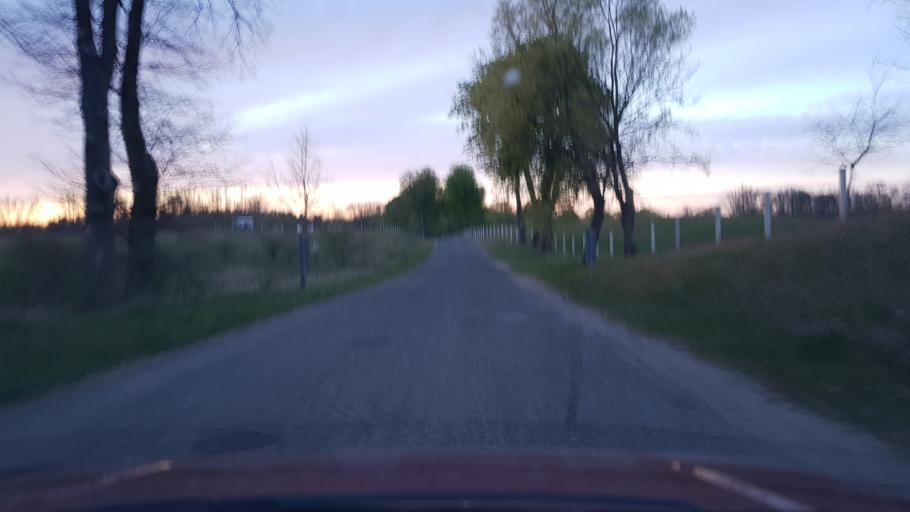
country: PL
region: West Pomeranian Voivodeship
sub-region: Powiat lobeski
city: Wegorzyno
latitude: 53.5129
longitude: 15.4474
